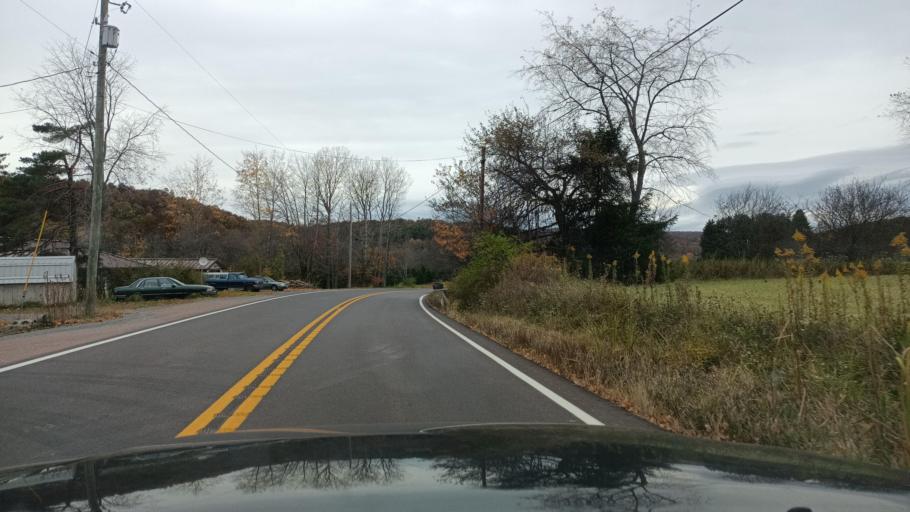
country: US
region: Maryland
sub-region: Garrett County
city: Oakland
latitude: 39.3124
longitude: -79.4809
